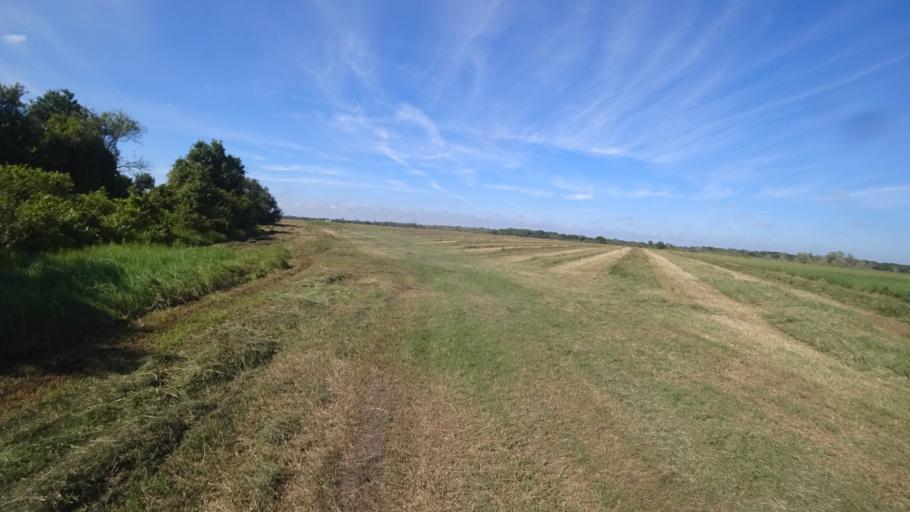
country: US
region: Florida
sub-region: DeSoto County
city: Nocatee
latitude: 27.2649
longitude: -82.0942
